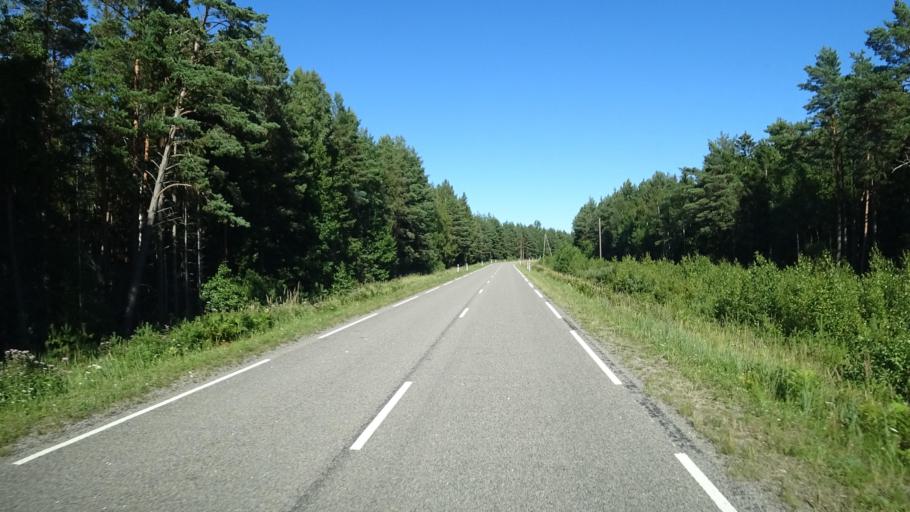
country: LV
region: Dundaga
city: Dundaga
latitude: 57.6759
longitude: 22.3314
